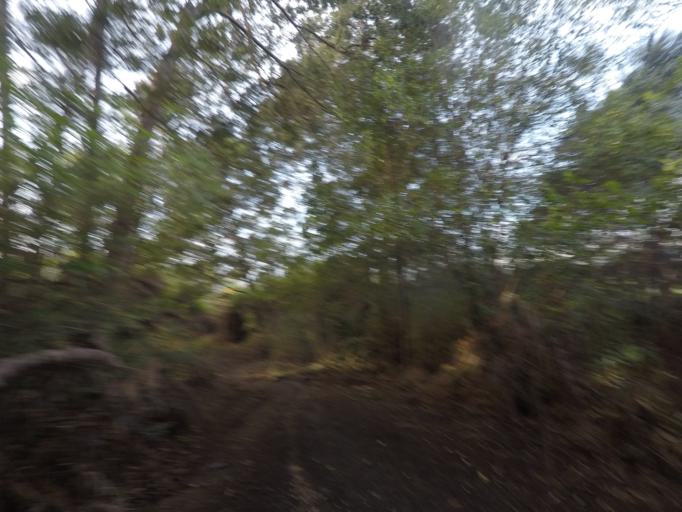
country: NZ
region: Auckland
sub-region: Auckland
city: Waitakere
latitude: -36.9023
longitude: 174.6427
